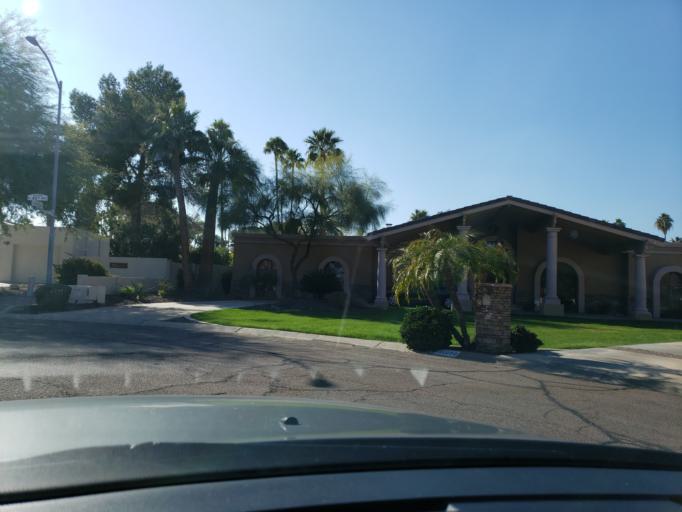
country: US
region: Arizona
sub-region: Maricopa County
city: Paradise Valley
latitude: 33.5890
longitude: -111.9838
